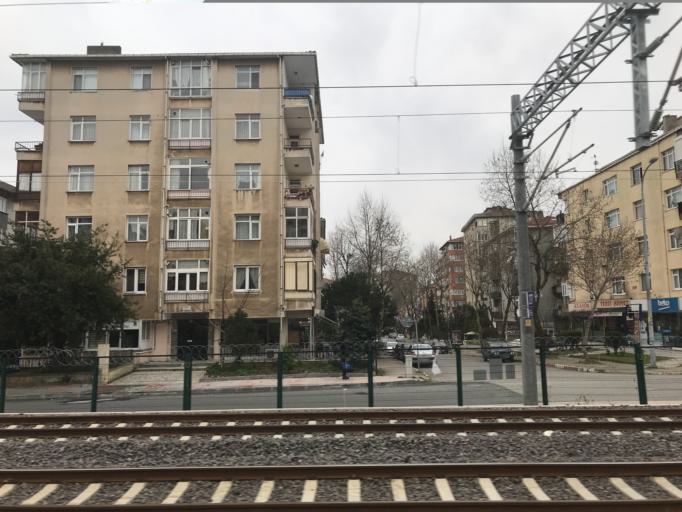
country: TR
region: Istanbul
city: Maltepe
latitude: 40.8970
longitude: 29.1715
